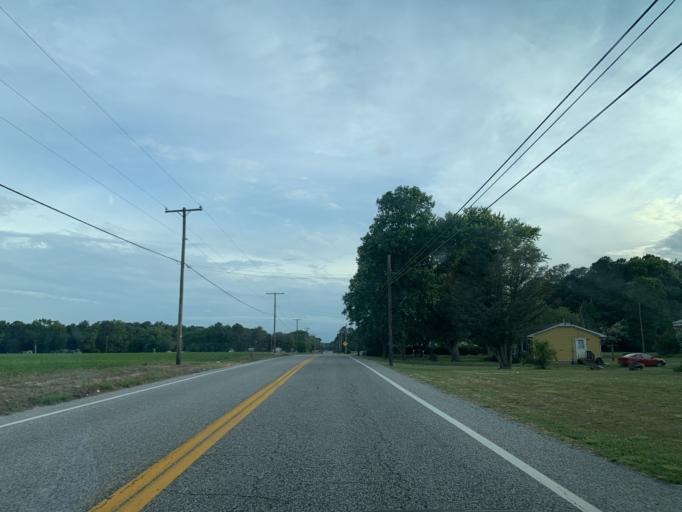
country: US
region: Maryland
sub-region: Worcester County
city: Snow Hill
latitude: 38.1529
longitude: -75.4071
